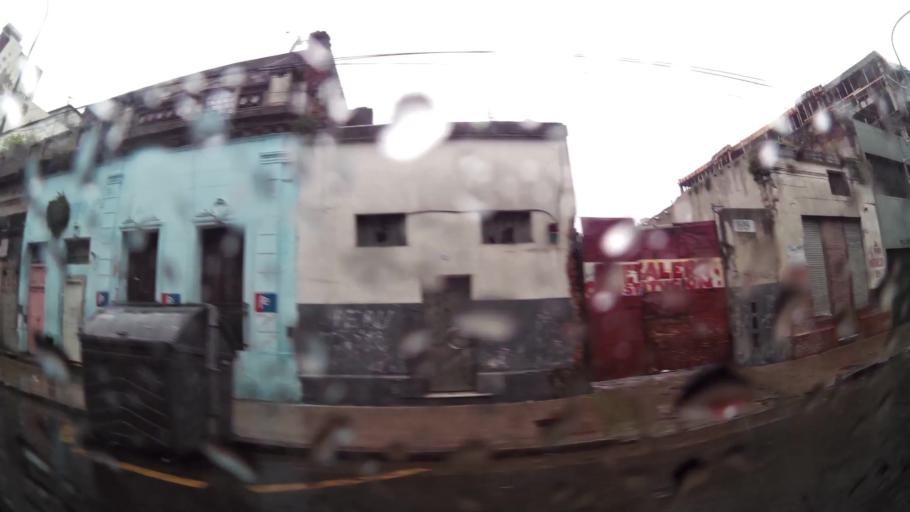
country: AR
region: Buenos Aires F.D.
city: Buenos Aires
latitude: -34.6293
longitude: -58.3843
